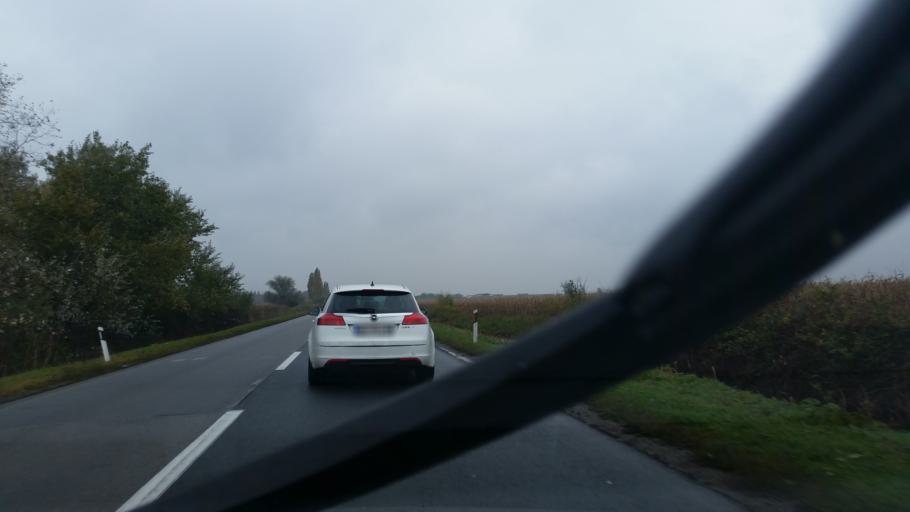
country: RS
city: Sefkerin
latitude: 44.9389
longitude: 20.4357
